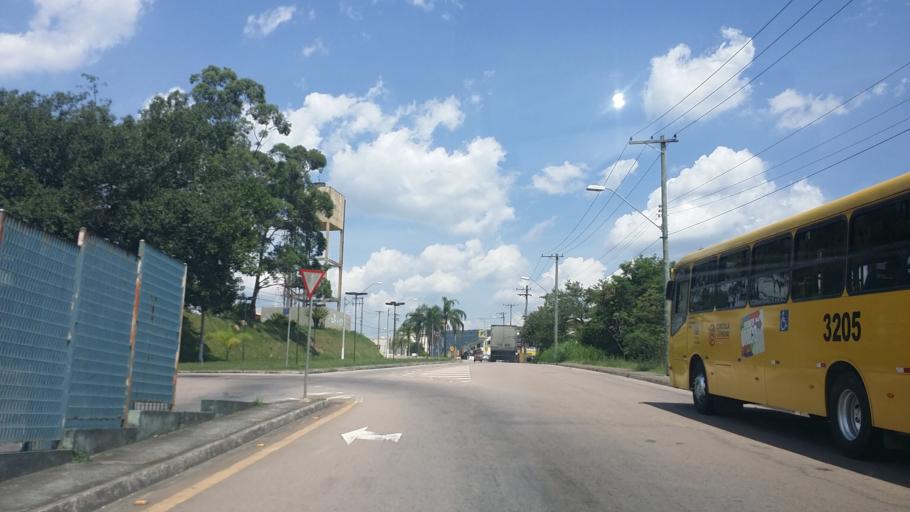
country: BR
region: Sao Paulo
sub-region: Jundiai
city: Jundiai
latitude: -23.1859
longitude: -46.9667
